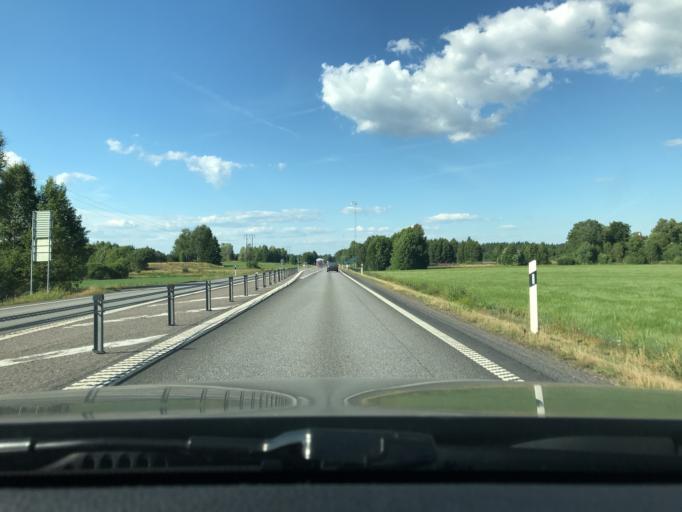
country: SE
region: Kronoberg
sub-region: Almhults Kommun
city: AElmhult
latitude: 56.4966
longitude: 14.1204
